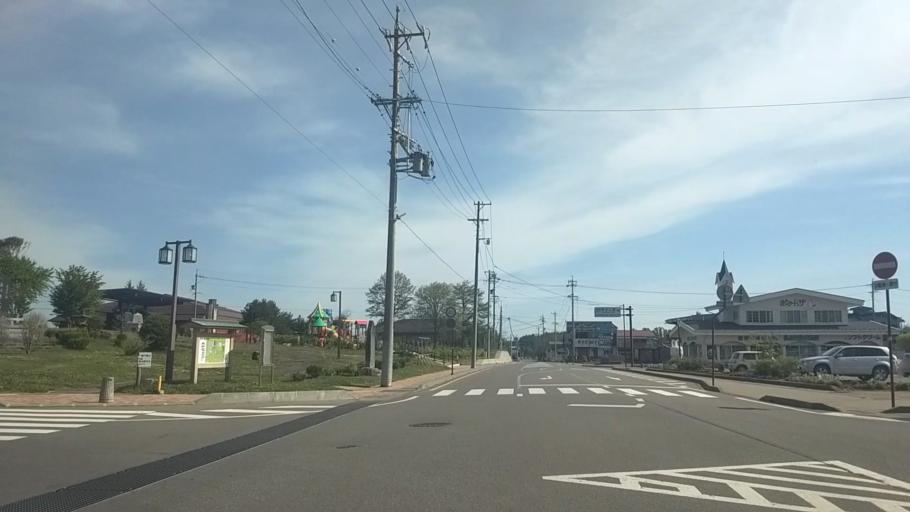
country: JP
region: Yamanashi
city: Nirasaki
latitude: 35.9551
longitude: 138.4737
